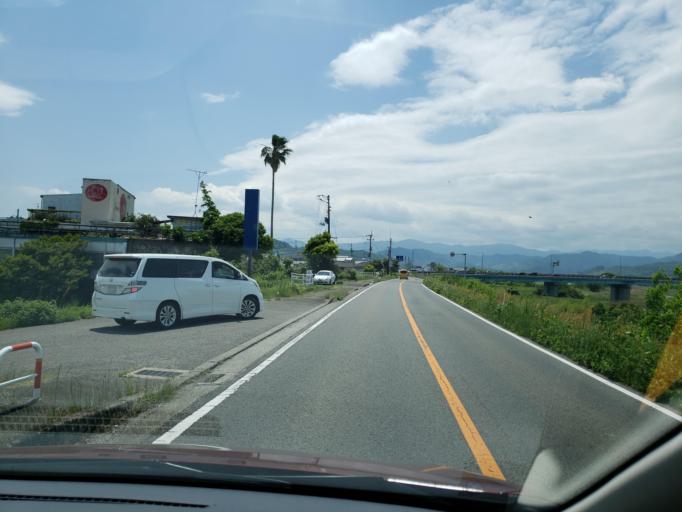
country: JP
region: Tokushima
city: Tokushima-shi
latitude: 34.0745
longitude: 134.5009
